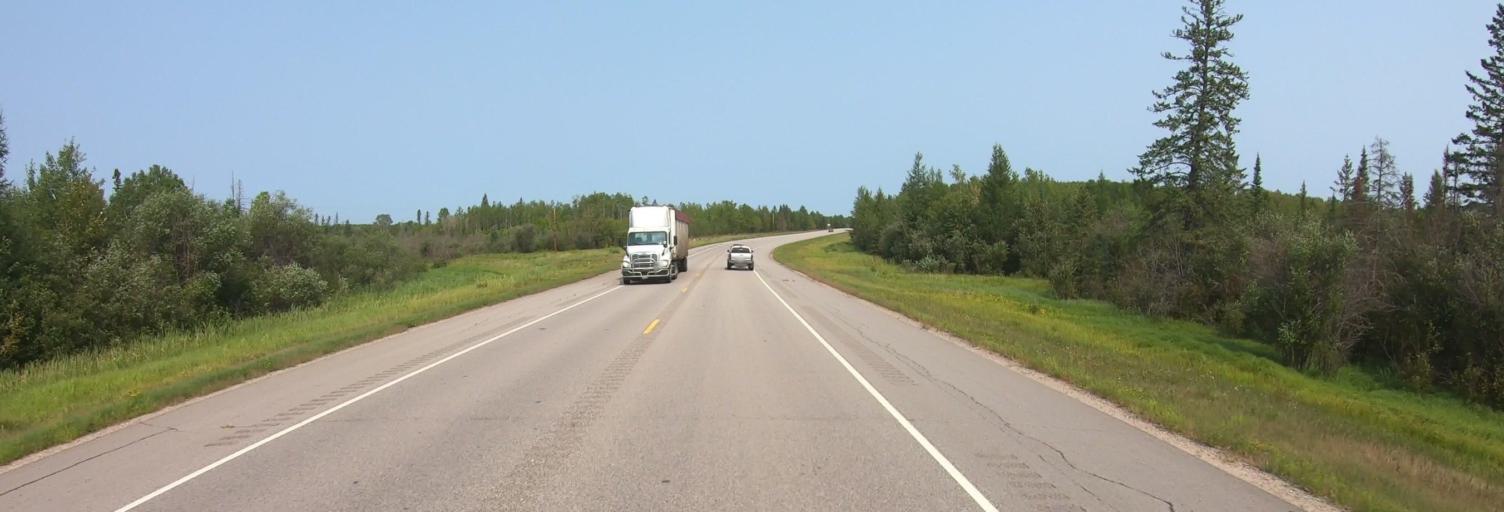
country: CA
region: Ontario
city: Fort Frances
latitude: 48.3296
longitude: -92.9622
